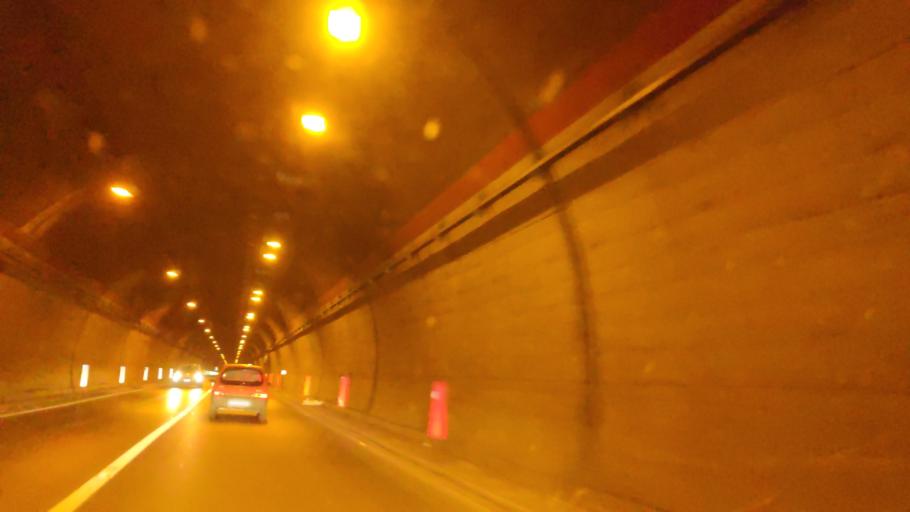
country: IT
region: Calabria
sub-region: Provincia di Cosenza
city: Amantea
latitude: 39.1031
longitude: 16.0811
